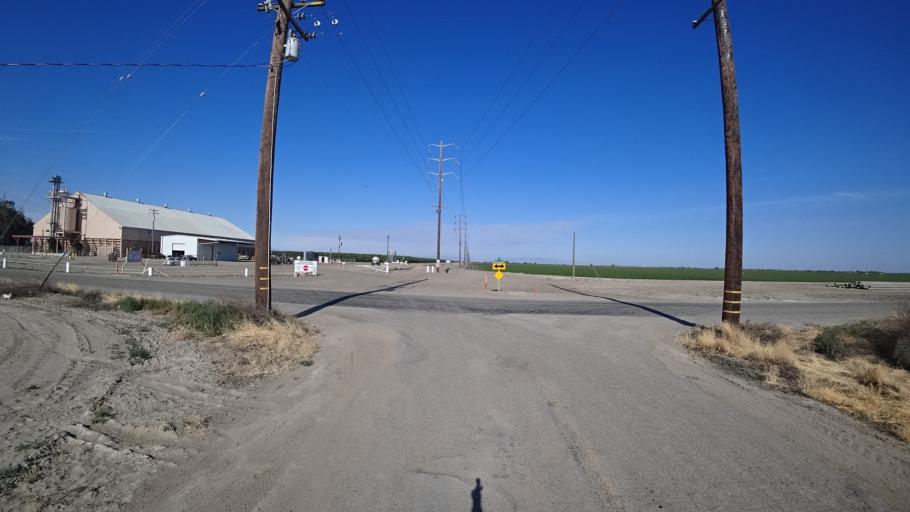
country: US
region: California
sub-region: Kings County
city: Stratford
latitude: 36.2261
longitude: -119.8341
